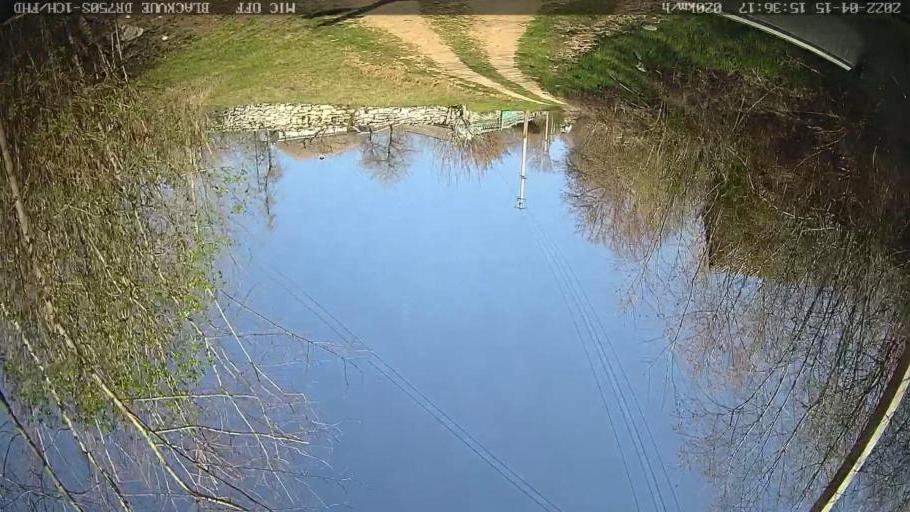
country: MD
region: Raionul Ocnita
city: Otaci
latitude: 48.3482
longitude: 27.9306
